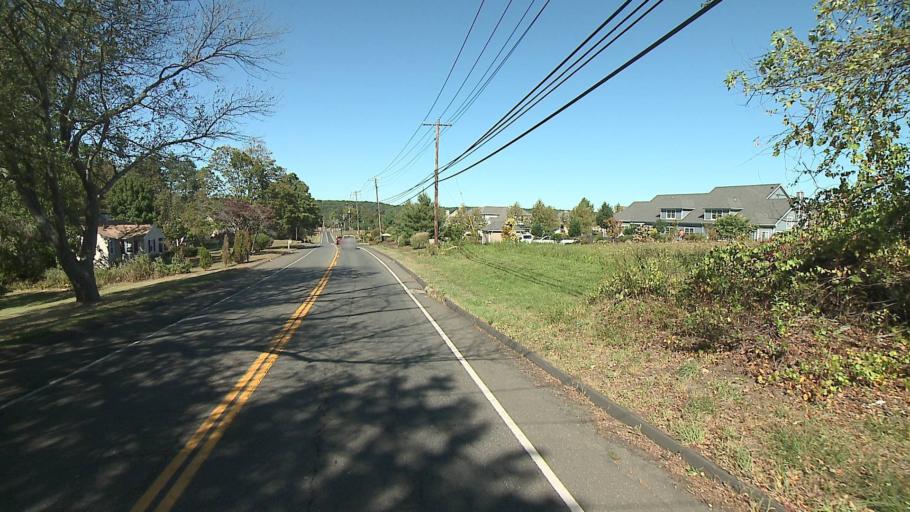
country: US
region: Connecticut
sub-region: New Haven County
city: Orange
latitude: 41.3070
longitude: -73.0452
